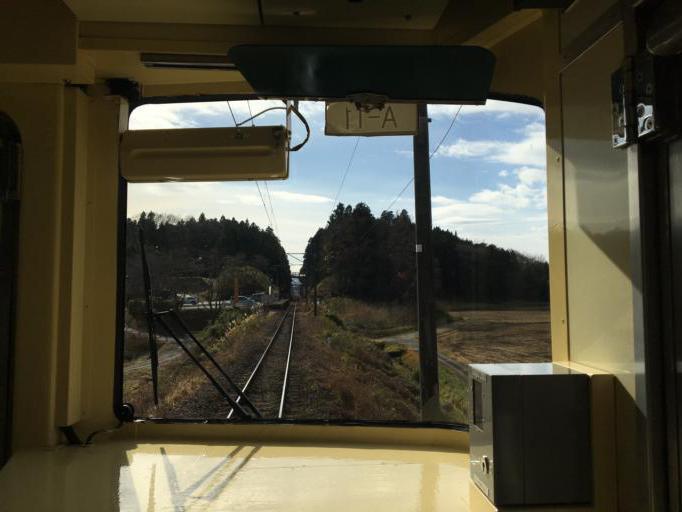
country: JP
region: Miyagi
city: Kakuda
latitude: 37.9979
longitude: 140.7762
